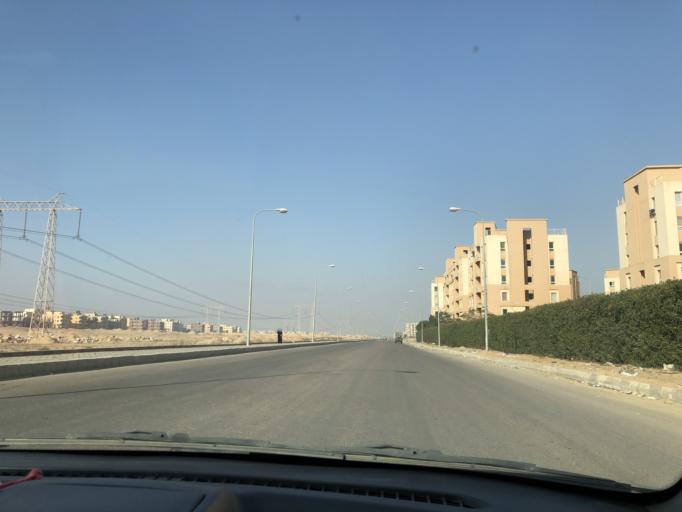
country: EG
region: Al Jizah
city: Madinat Sittah Uktubar
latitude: 29.9135
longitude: 31.0527
